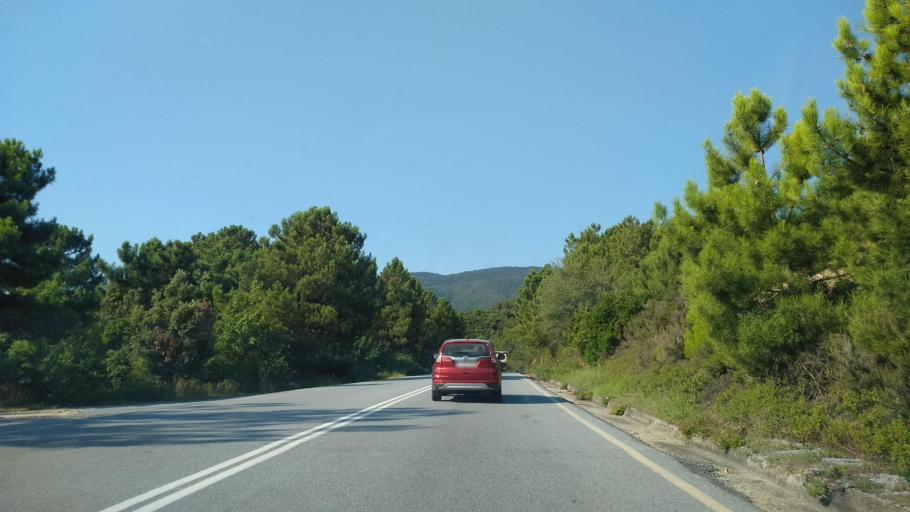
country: GR
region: Central Macedonia
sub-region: Nomos Chalkidikis
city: Stratonion
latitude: 40.5646
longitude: 23.8222
